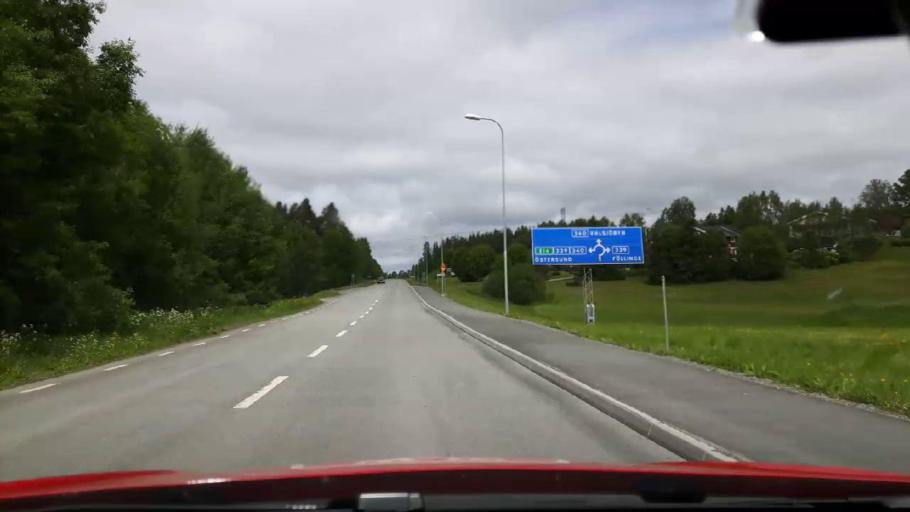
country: SE
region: Jaemtland
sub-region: Krokoms Kommun
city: Krokom
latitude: 63.3341
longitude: 14.4451
